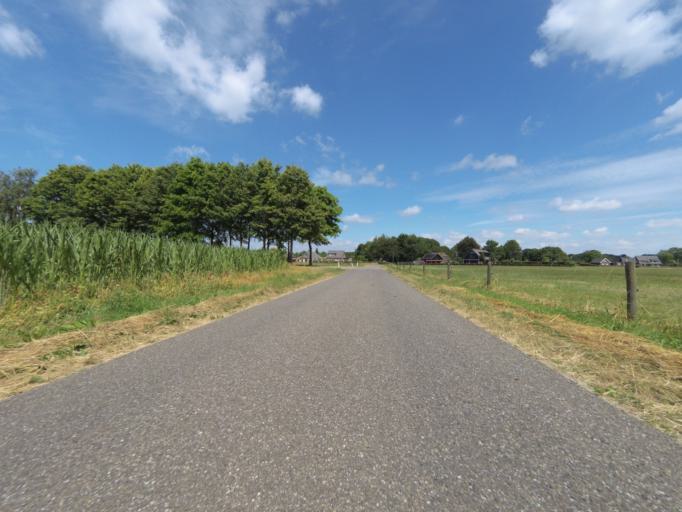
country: NL
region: Gelderland
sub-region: Gemeente Voorst
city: Twello
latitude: 52.2109
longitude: 6.1097
